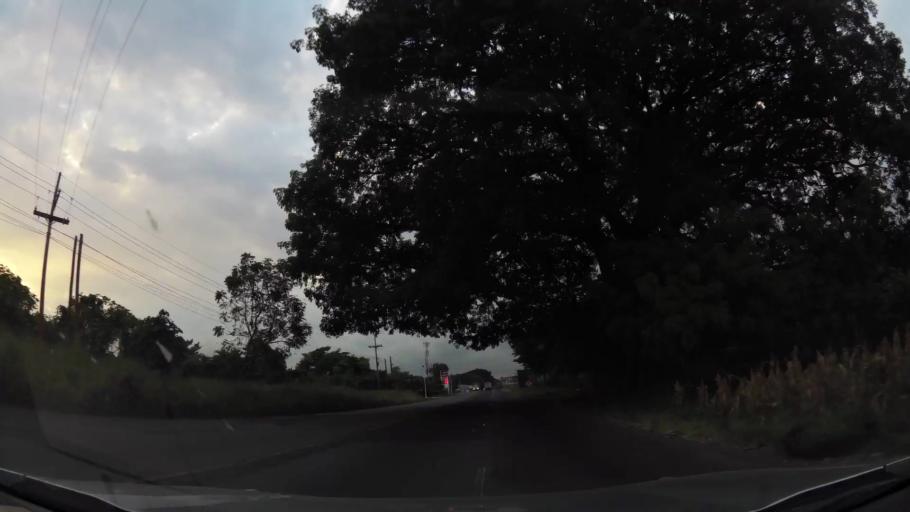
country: GT
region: Escuintla
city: Siquinala
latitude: 14.2865
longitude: -90.9377
